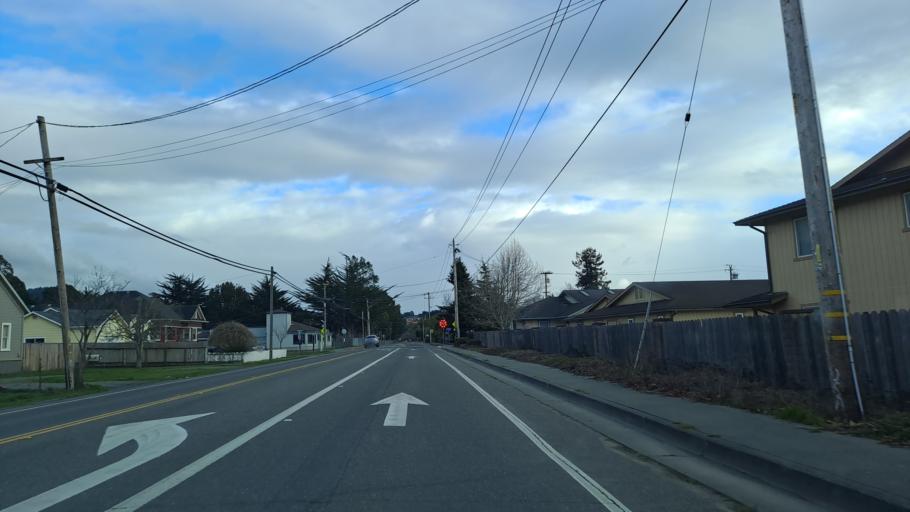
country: US
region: California
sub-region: Humboldt County
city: Fortuna
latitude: 40.5933
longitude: -124.1406
